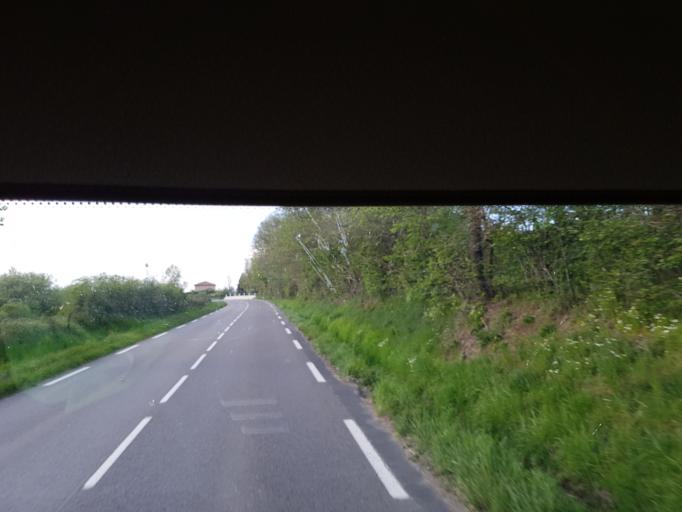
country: FR
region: Rhone-Alpes
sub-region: Departement du Rhone
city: Lentilly
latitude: 45.8043
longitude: 4.6684
